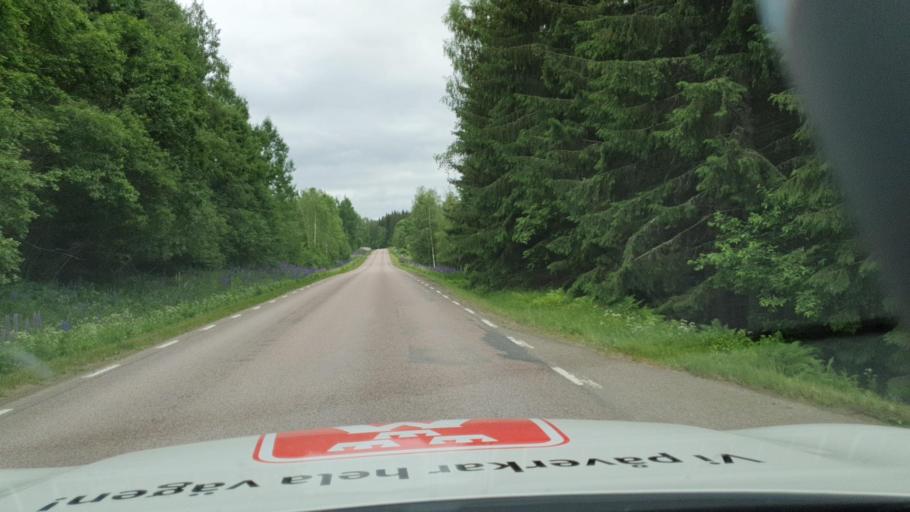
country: SE
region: Vaermland
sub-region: Torsby Kommun
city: Torsby
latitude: 59.9417
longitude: 12.7445
